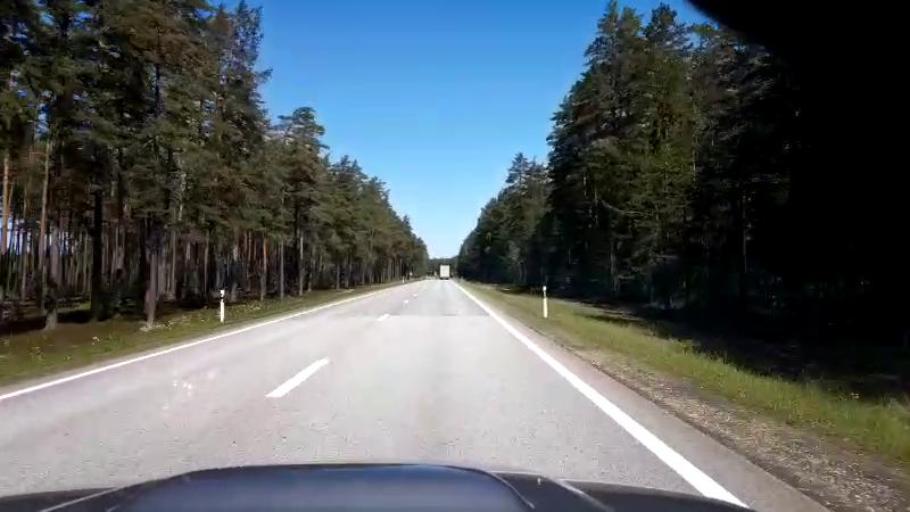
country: LV
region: Salacgrivas
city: Salacgriva
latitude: 57.5658
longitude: 24.4343
